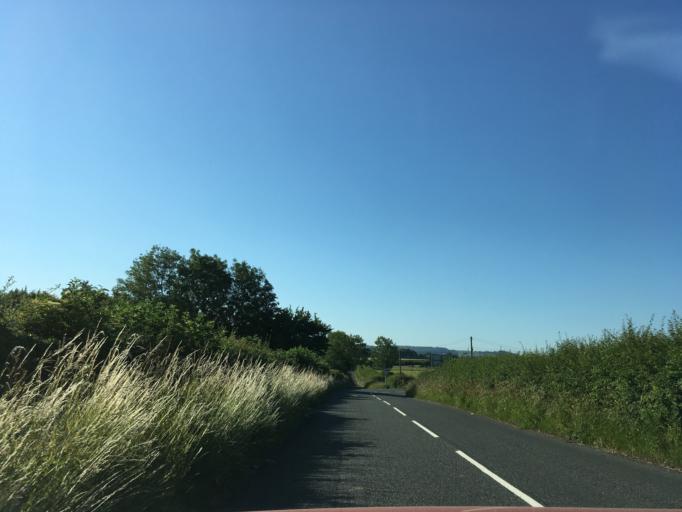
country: GB
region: England
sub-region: South Gloucestershire
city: Pucklechurch
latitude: 51.4680
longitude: -2.4255
